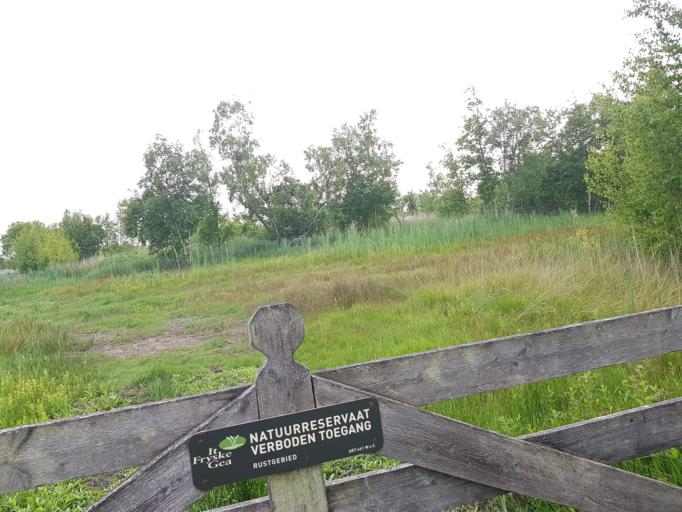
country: NL
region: Friesland
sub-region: Gemeente Tytsjerksteradiel
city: Garyp
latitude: 53.1363
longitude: 5.9394
